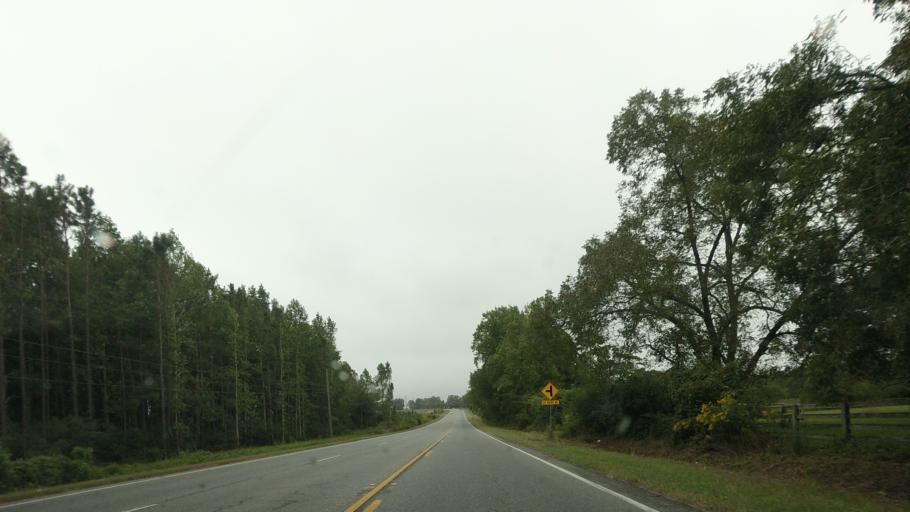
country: US
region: Georgia
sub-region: Ben Hill County
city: Fitzgerald
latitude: 31.6766
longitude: -83.2364
